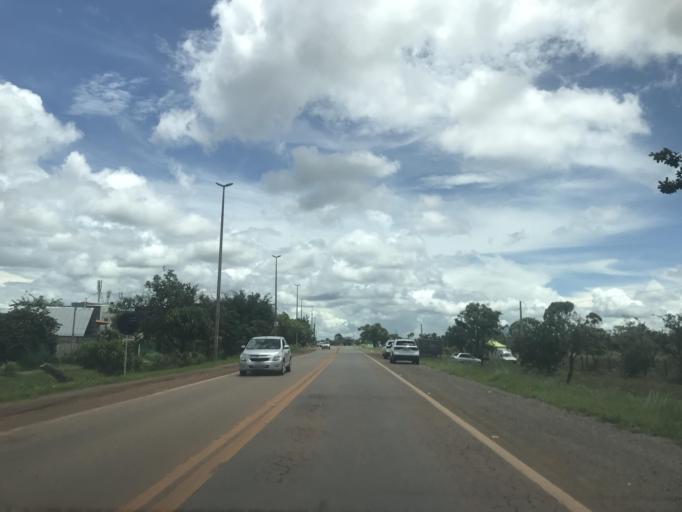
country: BR
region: Federal District
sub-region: Brasilia
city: Brasilia
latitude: -15.6921
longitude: -47.8284
